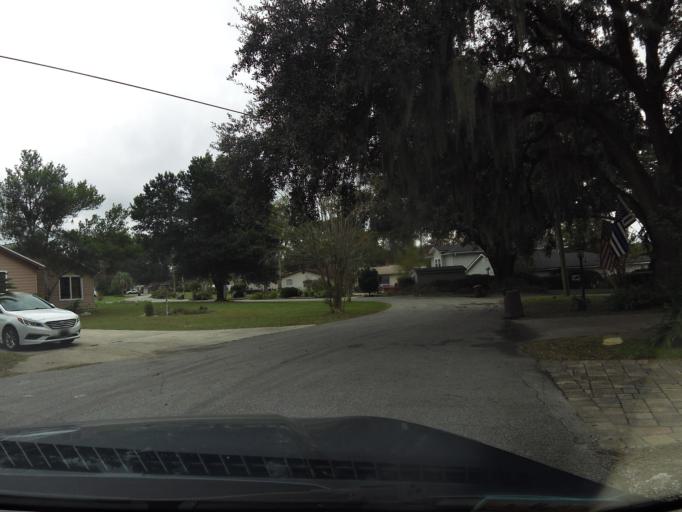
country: US
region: Florida
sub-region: Duval County
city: Jacksonville
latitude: 30.3069
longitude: -81.6078
